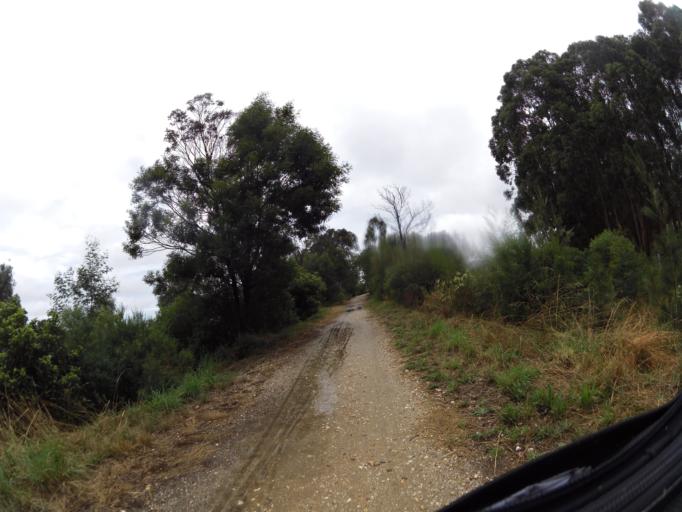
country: AU
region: Victoria
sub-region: East Gippsland
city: Bairnsdale
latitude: -37.8121
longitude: 147.7428
